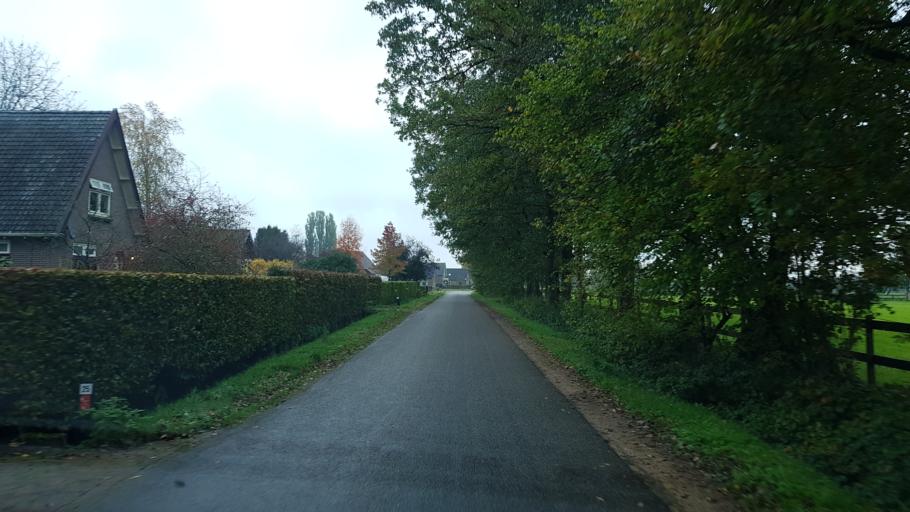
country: NL
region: Gelderland
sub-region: Gemeente Epe
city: Vaassen
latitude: 52.2496
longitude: 5.9594
